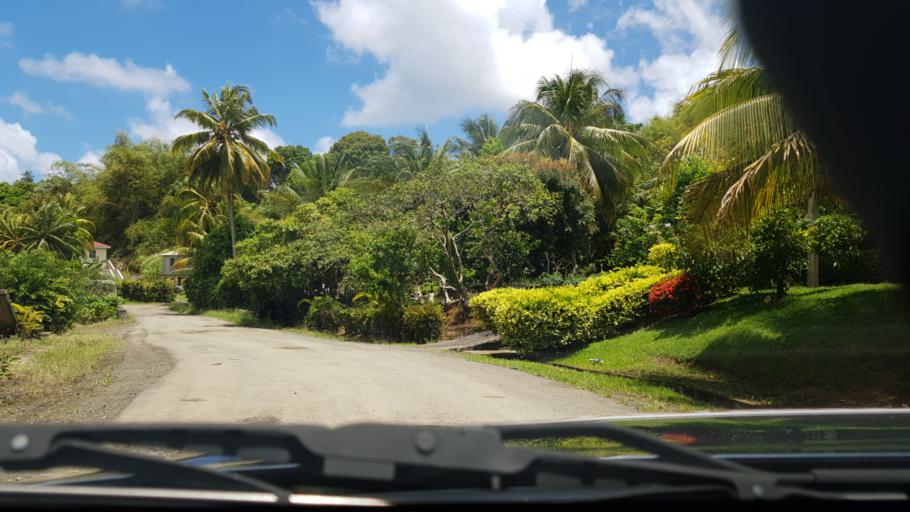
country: LC
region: Anse-la-Raye
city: Anse La Raye
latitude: 13.9522
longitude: -60.9964
